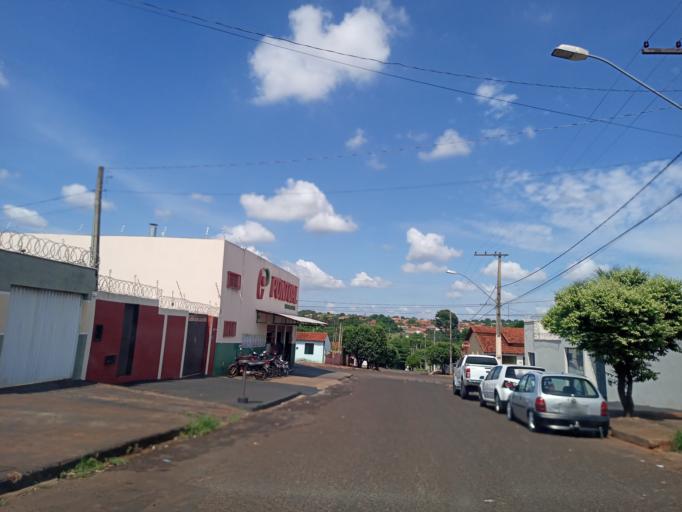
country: BR
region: Minas Gerais
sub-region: Ituiutaba
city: Ituiutaba
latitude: -18.9868
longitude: -49.4720
